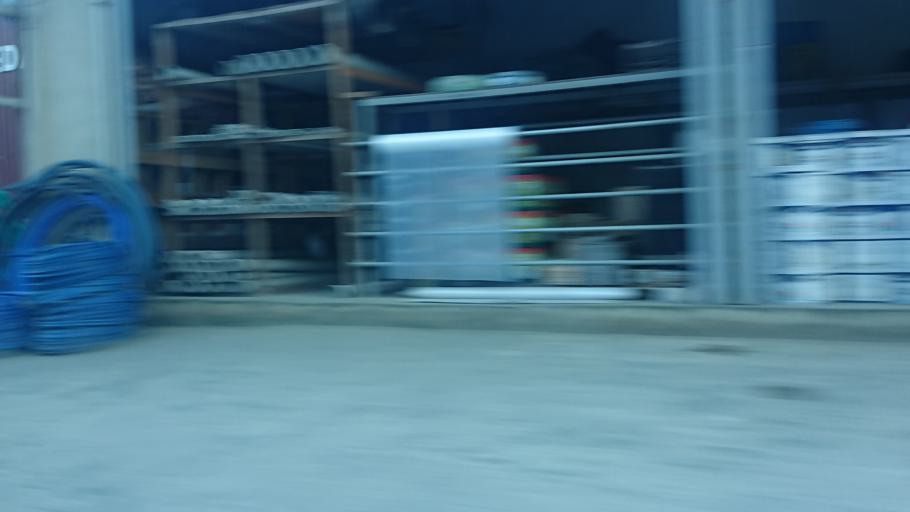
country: TR
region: Rize
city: Gundogdu
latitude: 41.0264
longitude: 40.5799
